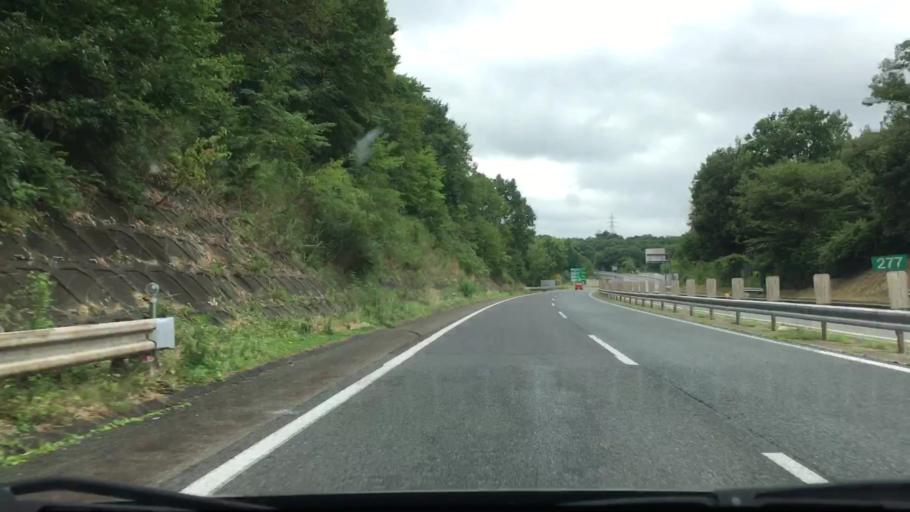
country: JP
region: Hiroshima
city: Shobara
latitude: 34.8457
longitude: 133.0204
